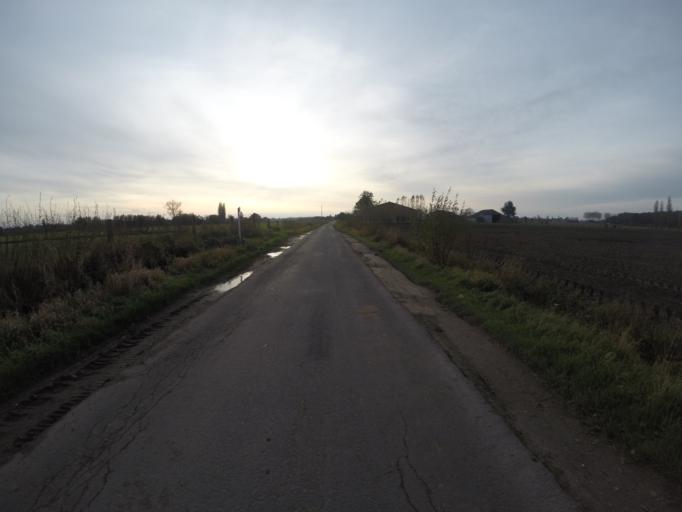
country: BE
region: Flanders
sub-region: Provincie Oost-Vlaanderen
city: Aalter
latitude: 51.0608
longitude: 3.4869
